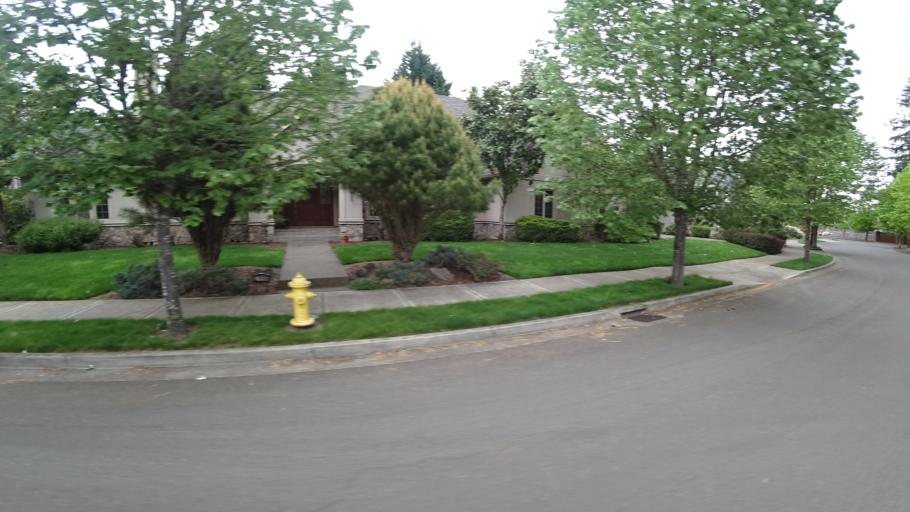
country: US
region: Oregon
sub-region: Washington County
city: Hillsboro
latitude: 45.5488
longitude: -122.9771
